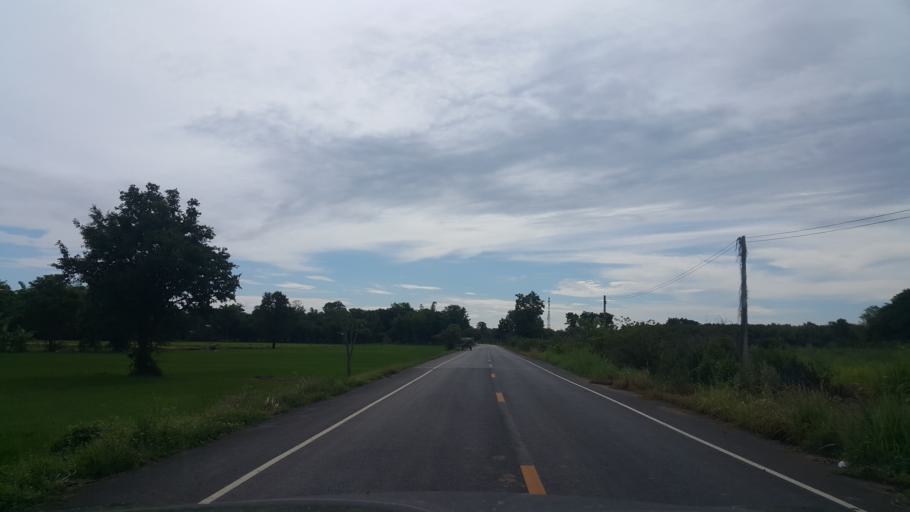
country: TH
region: Sukhothai
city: Si Nakhon
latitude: 17.2726
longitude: 99.9537
